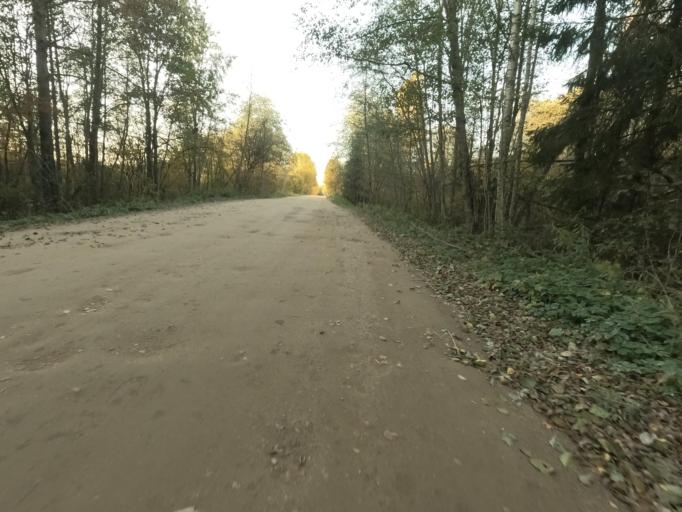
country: RU
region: Leningrad
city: Lyuban'
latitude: 59.0083
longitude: 31.0921
